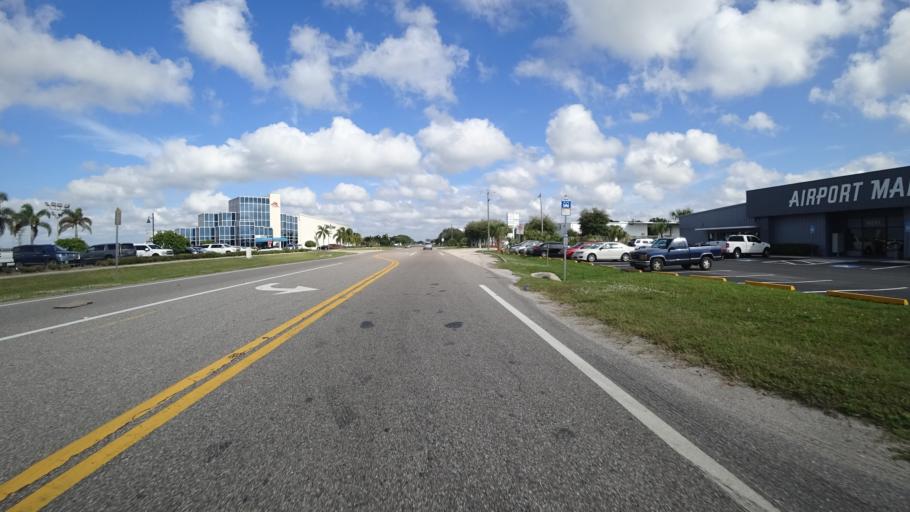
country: US
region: Florida
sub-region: Manatee County
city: Whitfield
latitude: 27.3923
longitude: -82.5468
